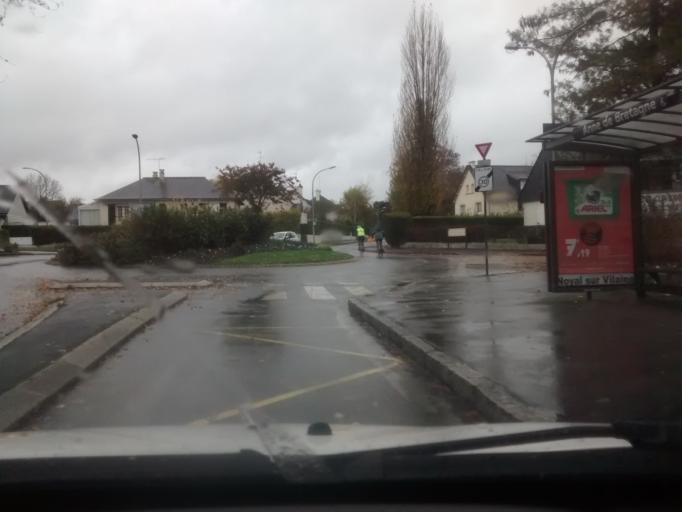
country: FR
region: Brittany
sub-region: Departement d'Ille-et-Vilaine
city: Fouillard
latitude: 48.1560
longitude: -1.5807
